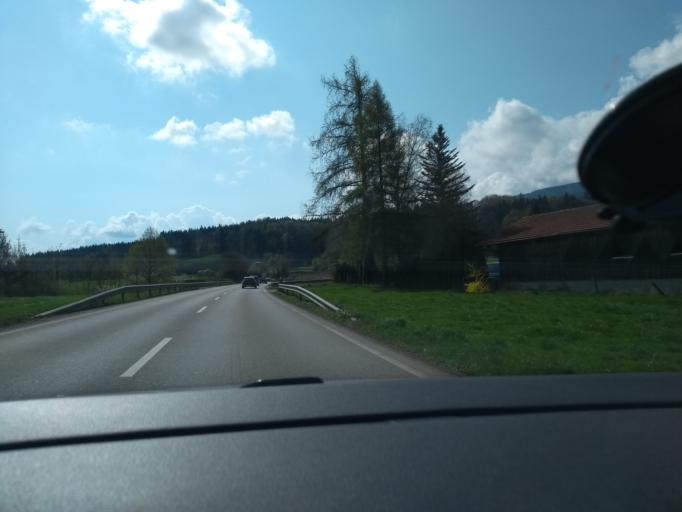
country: DE
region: Bavaria
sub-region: Upper Bavaria
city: Teisendorf
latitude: 47.8466
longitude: 12.8125
